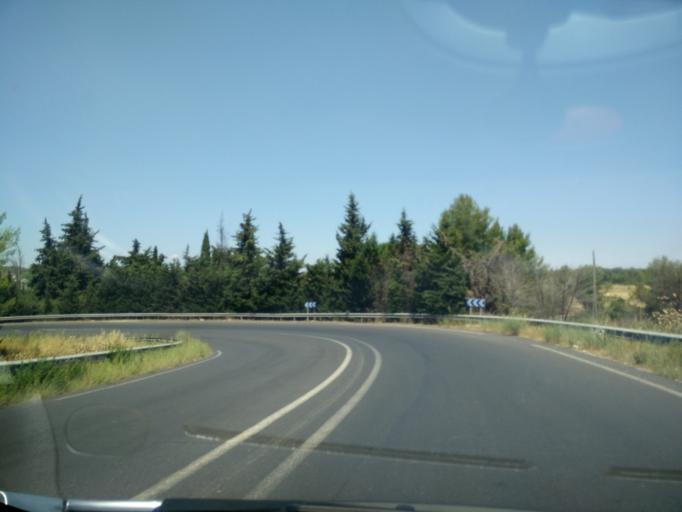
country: FR
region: Languedoc-Roussillon
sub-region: Departement de l'Herault
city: Lunel
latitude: 43.6965
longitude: 4.1308
